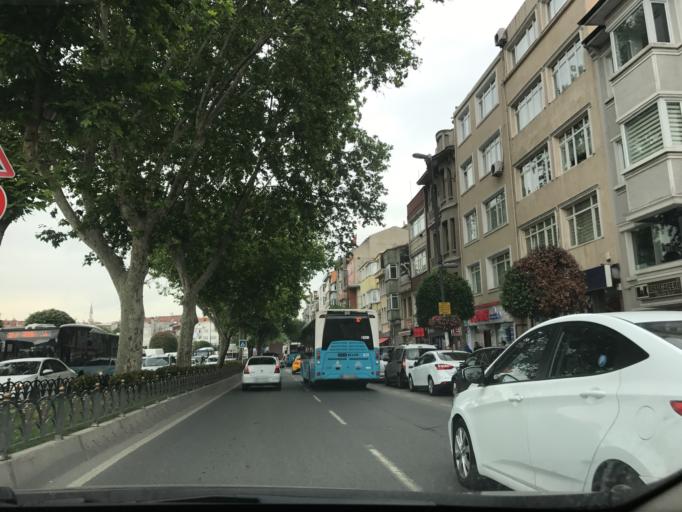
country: TR
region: Istanbul
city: Istanbul
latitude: 41.0281
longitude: 28.9378
